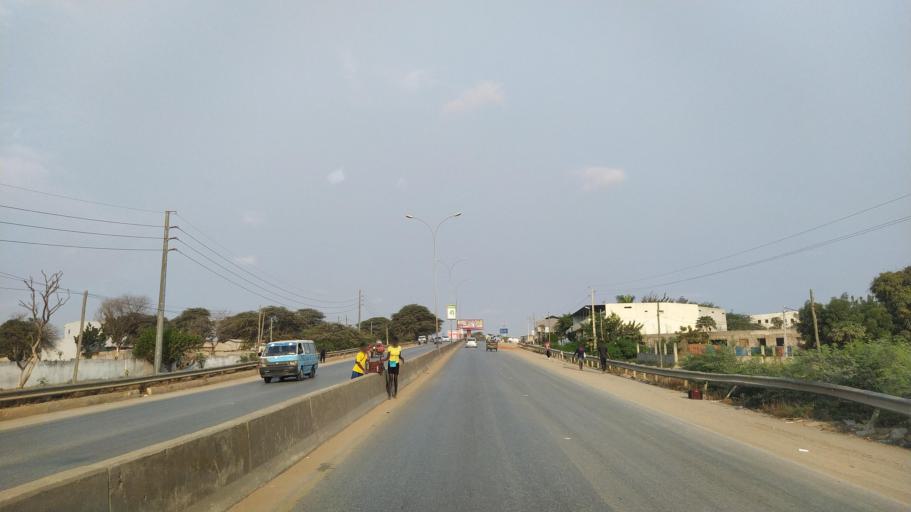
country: AO
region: Luanda
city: Luanda
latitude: -8.9197
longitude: 13.2198
